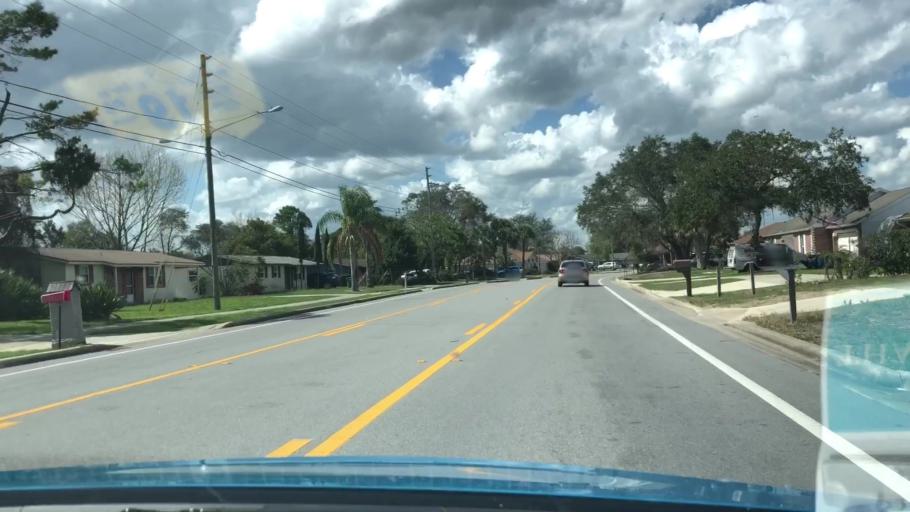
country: US
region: Florida
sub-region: Volusia County
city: Deltona
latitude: 28.8822
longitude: -81.2363
